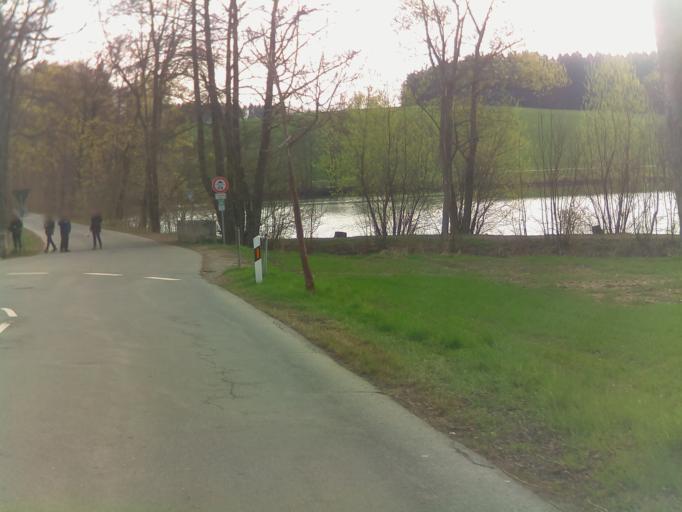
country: DE
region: Bavaria
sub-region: Upper Franconia
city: Hof
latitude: 50.2982
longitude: 11.8883
